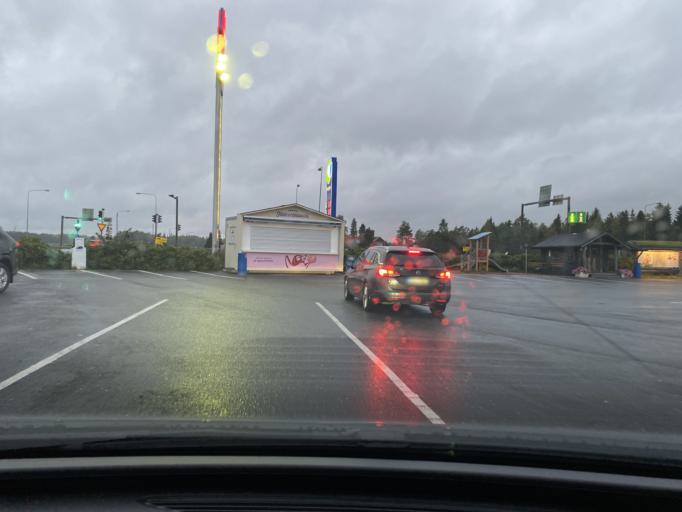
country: FI
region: Satakunta
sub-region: Pori
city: Huittinen
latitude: 61.1748
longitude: 22.6810
